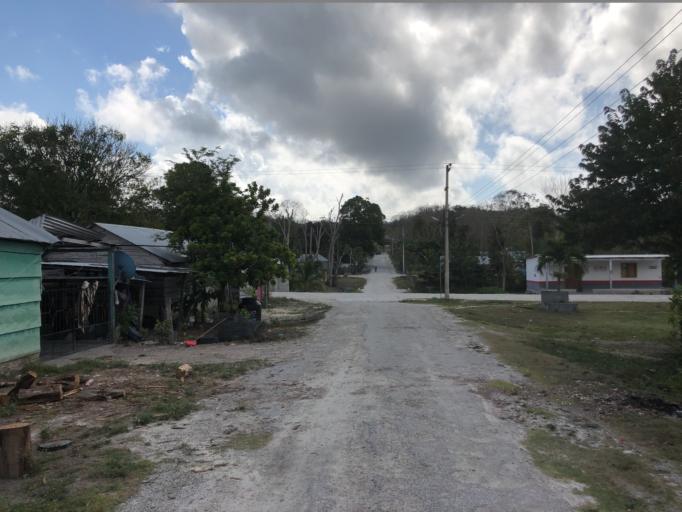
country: MX
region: Quintana Roo
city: Nicolas Bravo
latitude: 18.4522
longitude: -89.3071
